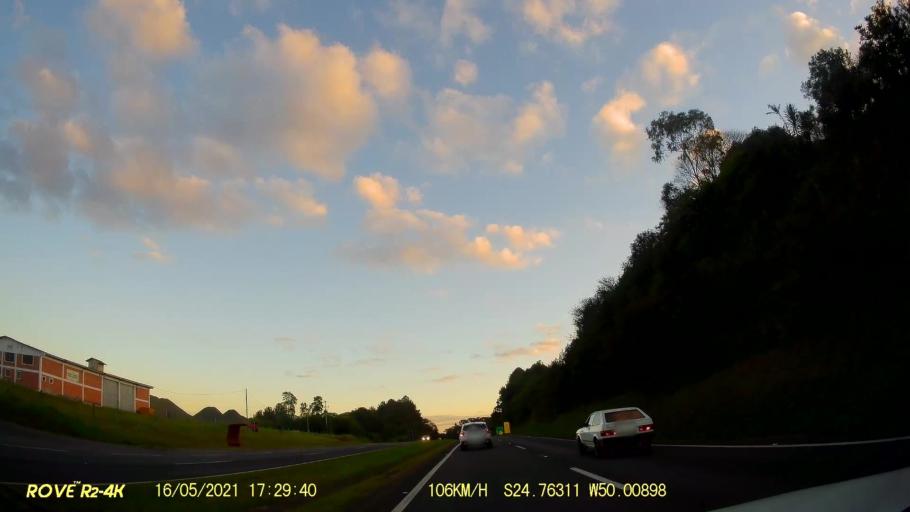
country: BR
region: Parana
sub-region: Castro
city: Castro
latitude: -24.7634
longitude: -50.0091
